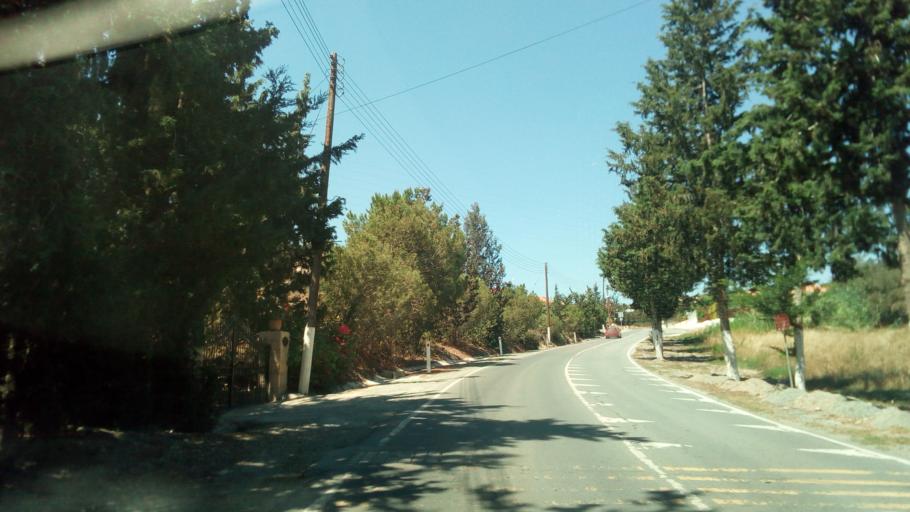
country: CY
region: Limassol
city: Pyrgos
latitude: 34.7333
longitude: 33.1748
